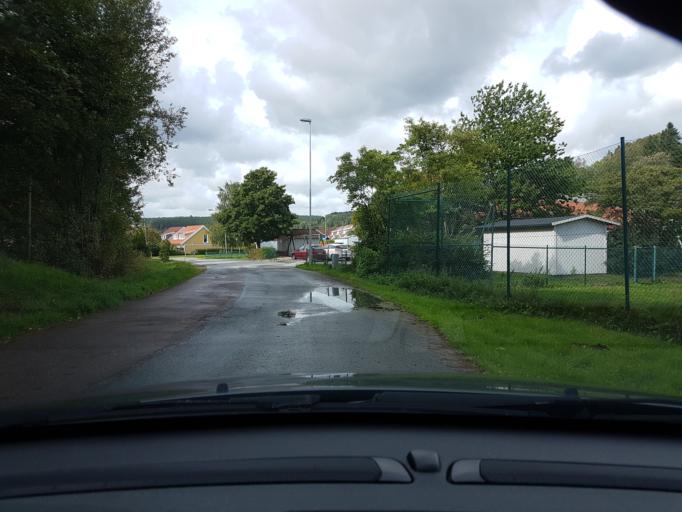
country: SE
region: Vaestra Goetaland
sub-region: Ale Kommun
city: Nodinge-Nol
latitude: 57.9078
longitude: 12.0632
